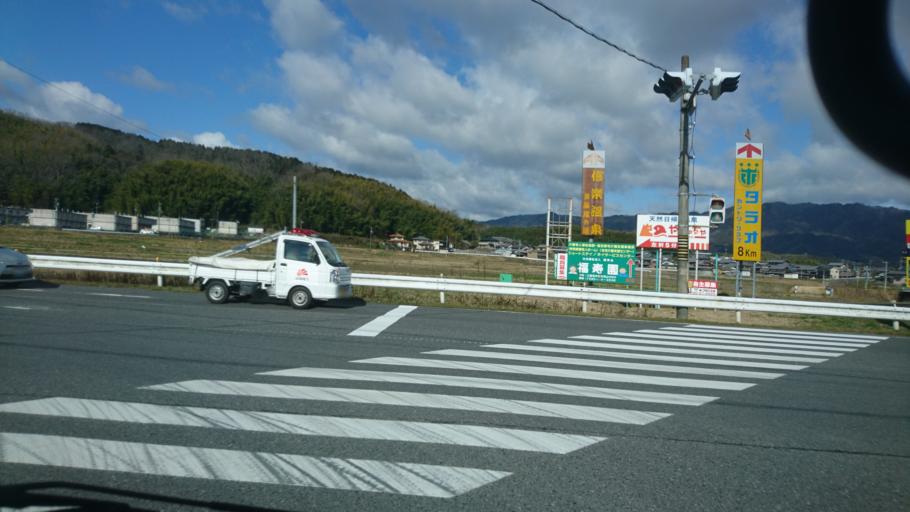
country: JP
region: Mie
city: Ueno-ebisumachi
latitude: 34.7705
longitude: 136.1070
